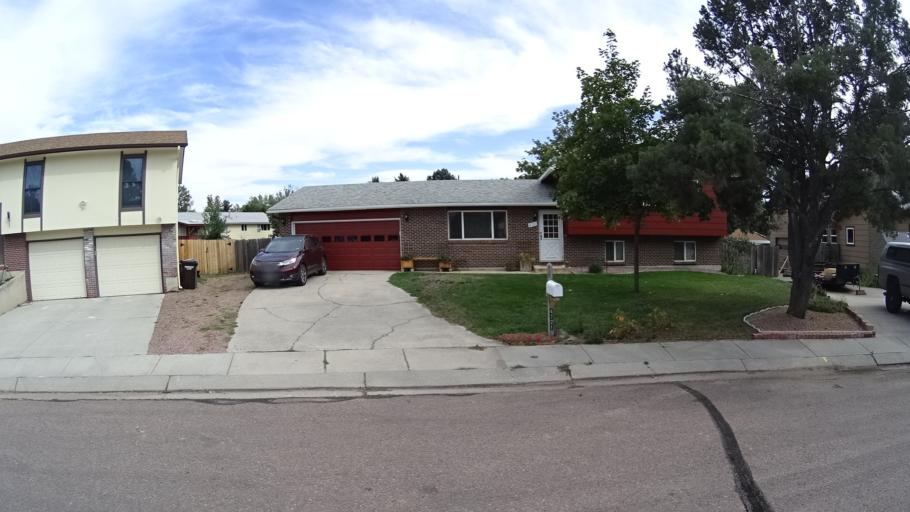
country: US
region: Colorado
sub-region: El Paso County
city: Colorado Springs
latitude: 38.9008
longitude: -104.7752
